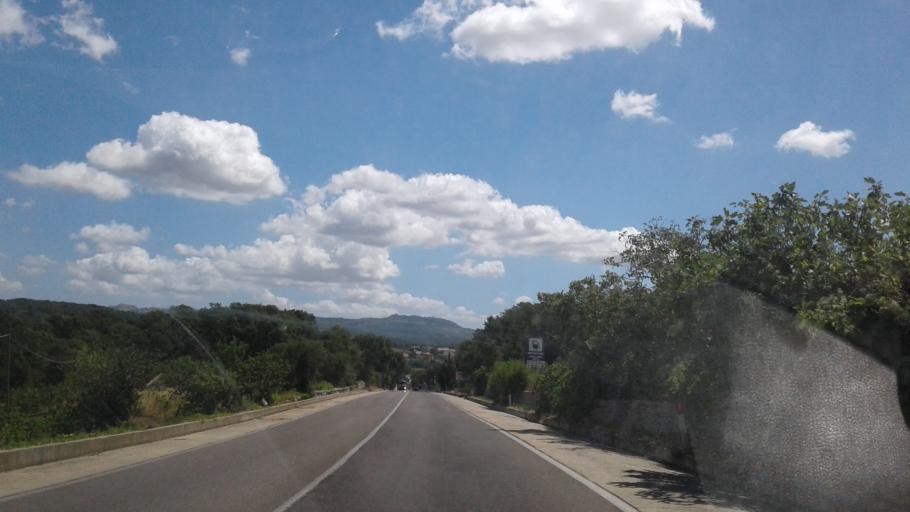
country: IT
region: Sardinia
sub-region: Provincia di Olbia-Tempio
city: Tempio Pausania
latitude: 40.9064
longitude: 9.1328
